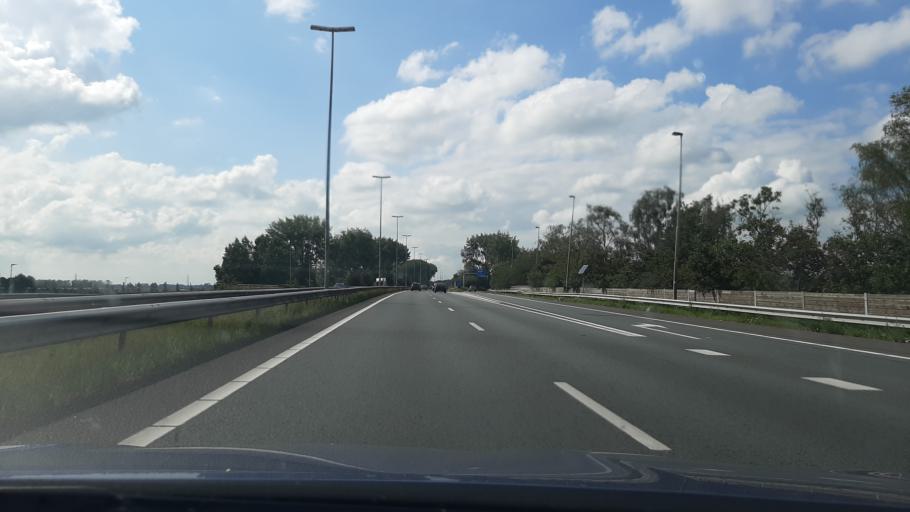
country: NL
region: Groningen
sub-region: Gemeente Groningen
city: Groningen
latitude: 53.1982
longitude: 6.5176
